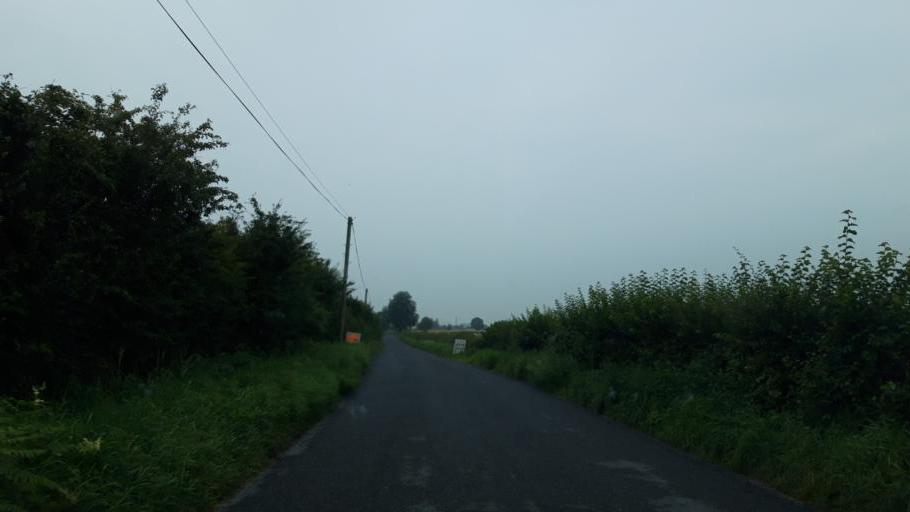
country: IE
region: Leinster
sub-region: Kilkenny
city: Thomastown
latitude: 52.6006
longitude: -7.1484
